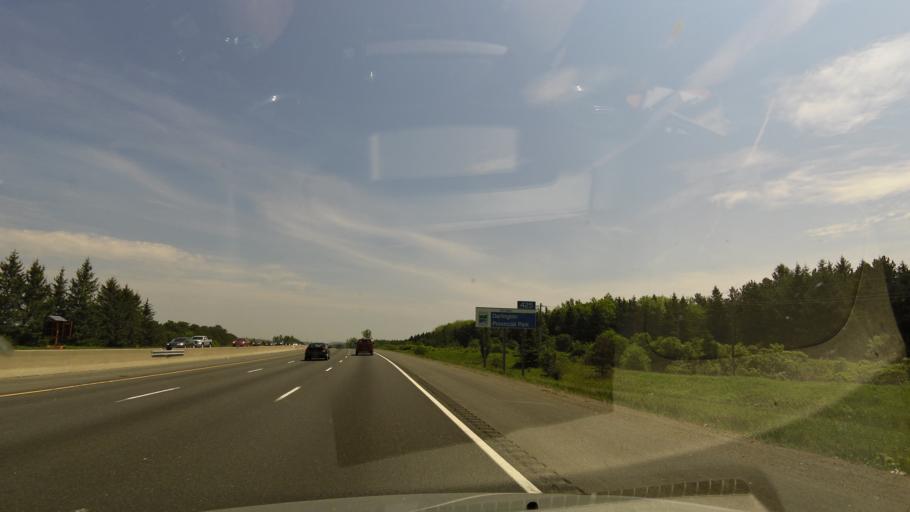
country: CA
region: Ontario
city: Oshawa
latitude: 43.8753
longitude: -78.7903
